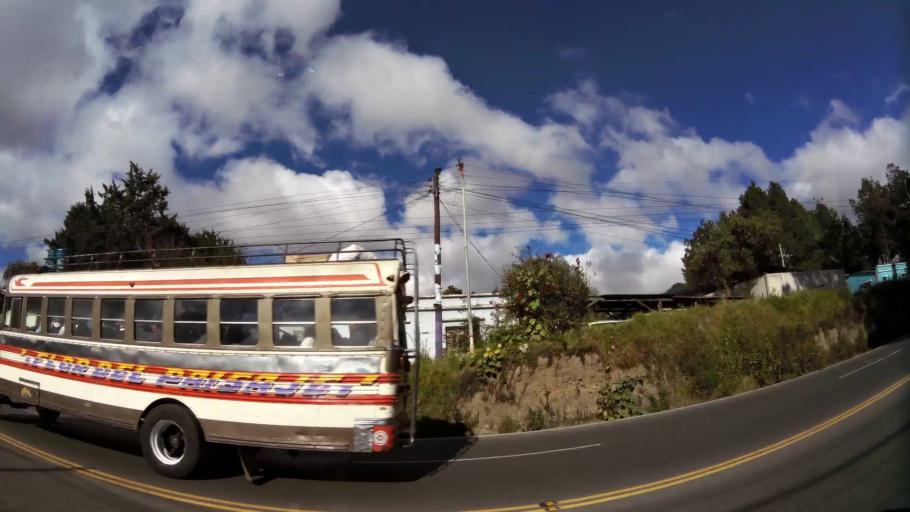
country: GT
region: Quetzaltenango
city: Salcaja
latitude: 14.8946
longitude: -91.4543
